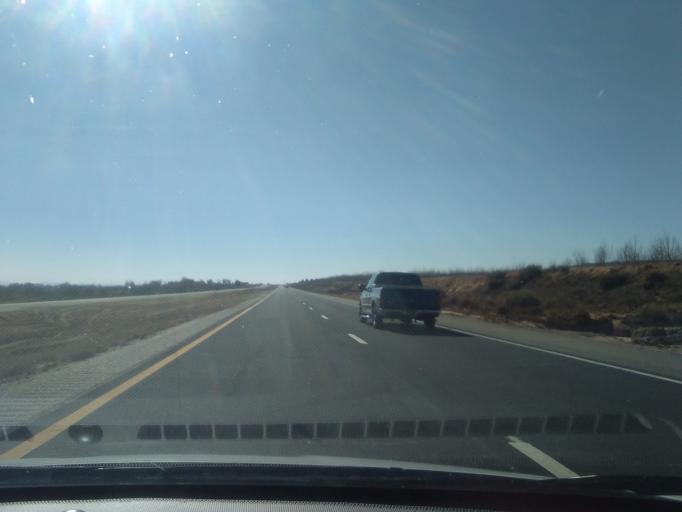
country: US
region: New Mexico
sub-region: Valencia County
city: Jarales
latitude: 34.6079
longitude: -106.7865
